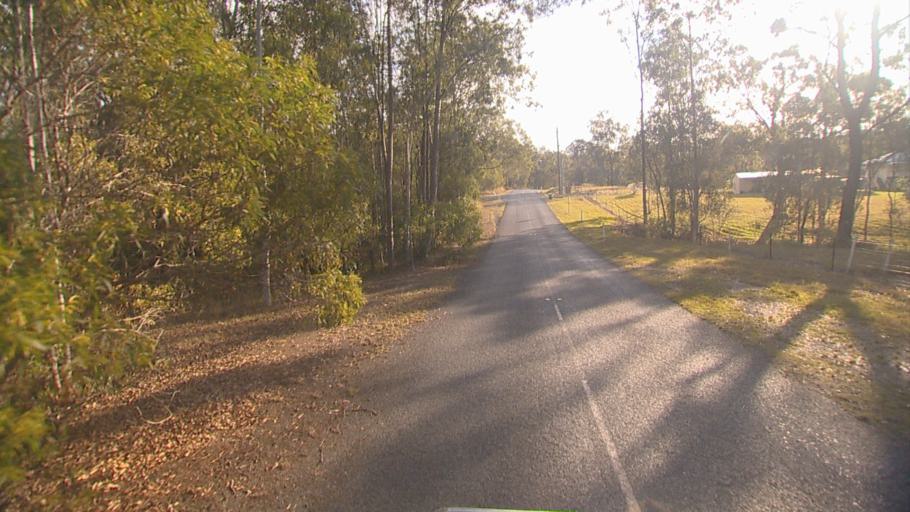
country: AU
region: Queensland
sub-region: Logan
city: Cedar Vale
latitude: -27.8457
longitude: 153.0839
